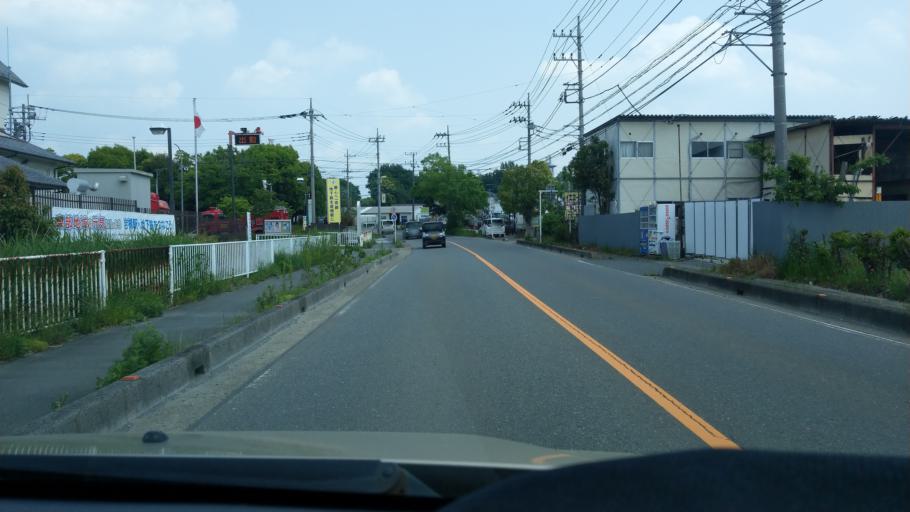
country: JP
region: Saitama
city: Iwatsuki
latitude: 35.9152
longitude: 139.7154
